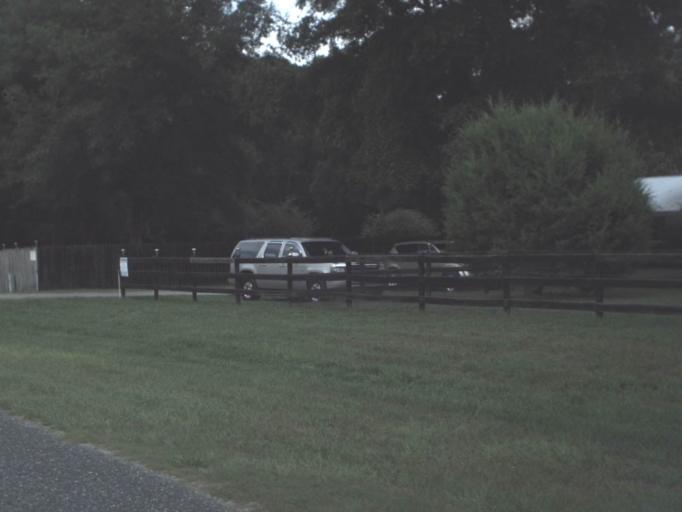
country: US
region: Florida
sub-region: Gilchrist County
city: Trenton
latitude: 29.5542
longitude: -82.8229
